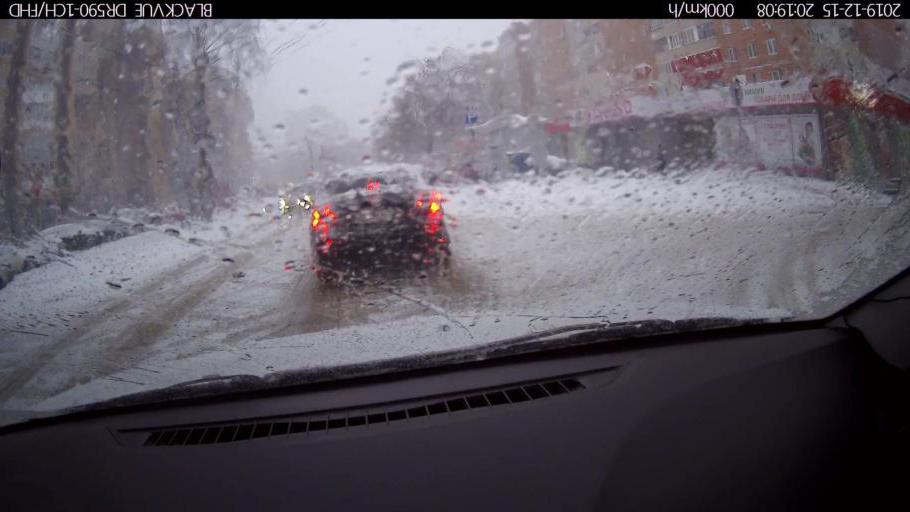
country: RU
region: Nizjnij Novgorod
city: Nizhniy Novgorod
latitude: 56.3166
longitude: 44.0245
